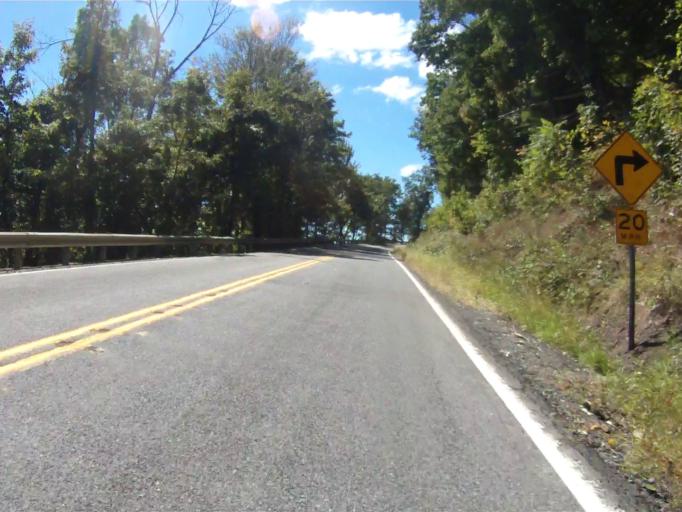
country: US
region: Pennsylvania
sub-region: Centre County
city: Park Forest Village
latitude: 40.9282
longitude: -77.9409
